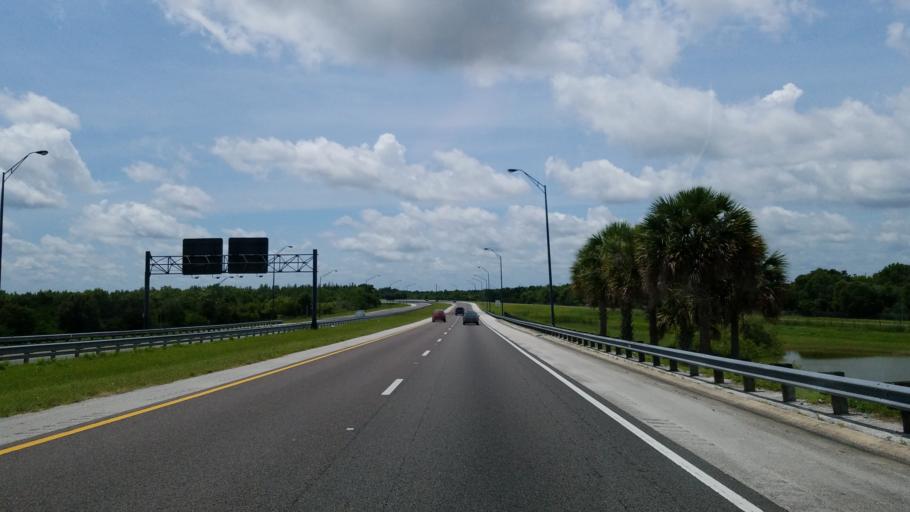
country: US
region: Florida
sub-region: Polk County
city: Winston
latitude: 28.0277
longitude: -82.0402
